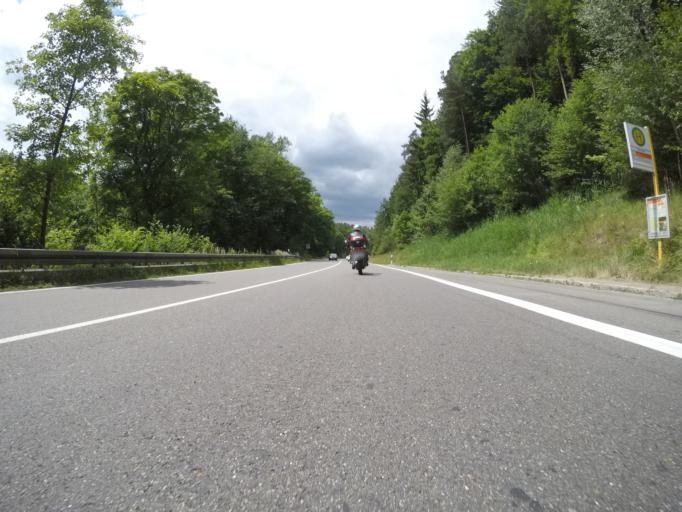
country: DE
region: Baden-Wuerttemberg
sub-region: Regierungsbezirk Stuttgart
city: Gerlingen
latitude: 48.7573
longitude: 9.0688
